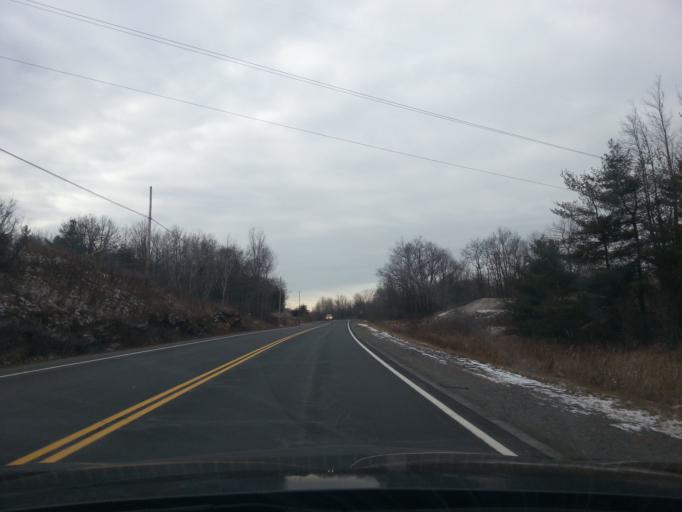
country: CA
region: Ontario
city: Deseronto
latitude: 44.5996
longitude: -77.1872
